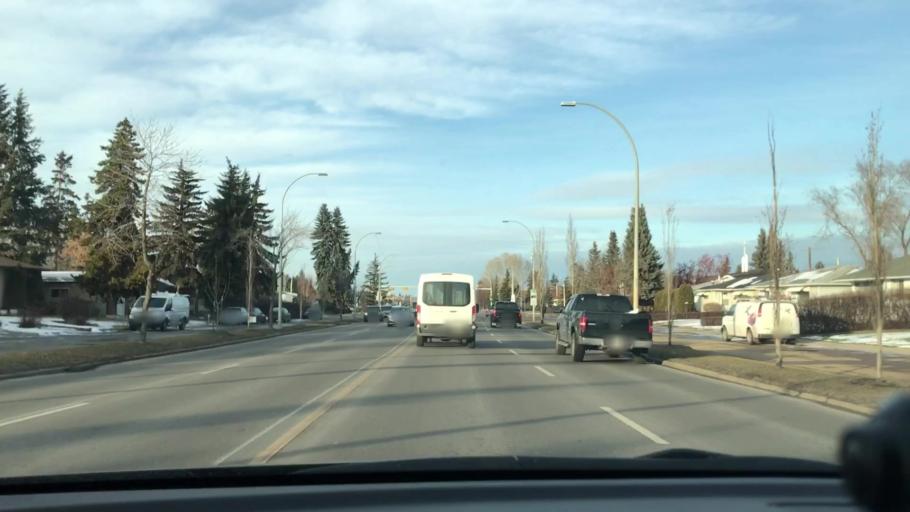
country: CA
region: Alberta
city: Edmonton
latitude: 53.5356
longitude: -113.4429
